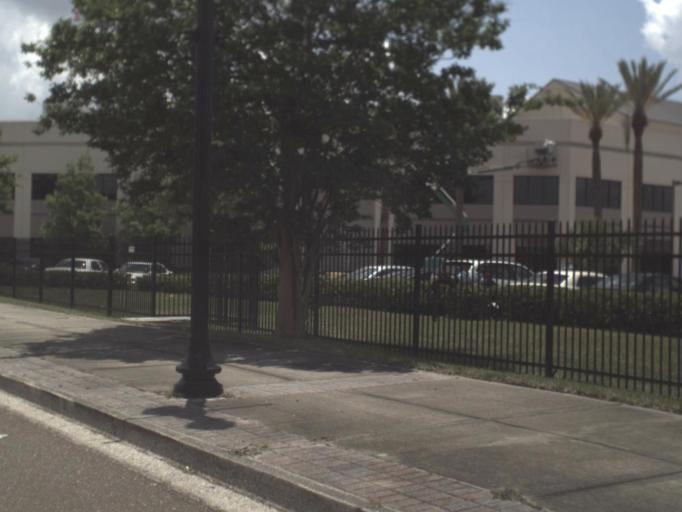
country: US
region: Florida
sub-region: Duval County
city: Jacksonville
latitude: 30.3286
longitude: -81.6685
